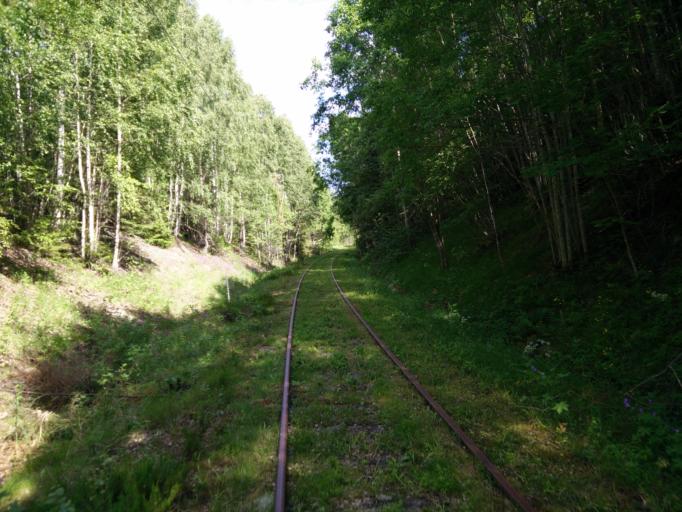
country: SE
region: Gaevleborg
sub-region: Hudiksvalls Kommun
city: Delsbo
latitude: 61.7978
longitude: 16.3788
